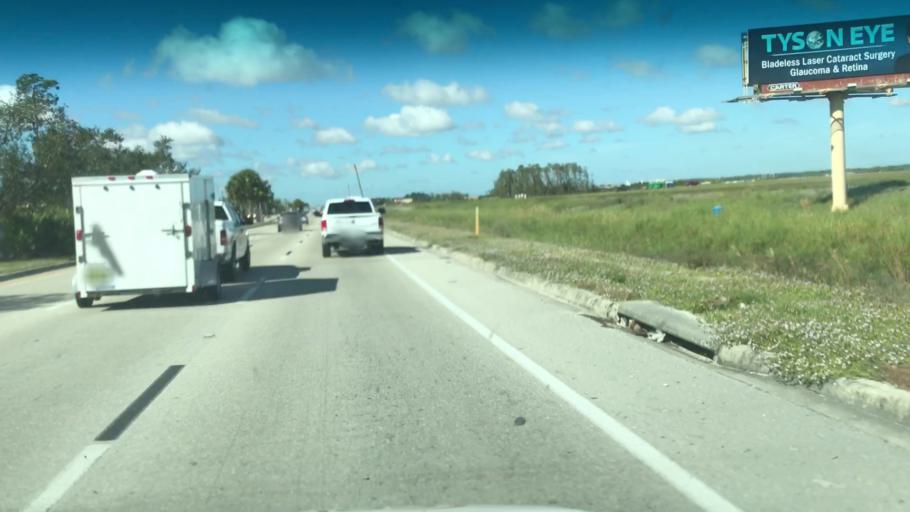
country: US
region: Florida
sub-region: Lee County
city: Three Oaks
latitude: 26.4929
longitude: -81.8036
